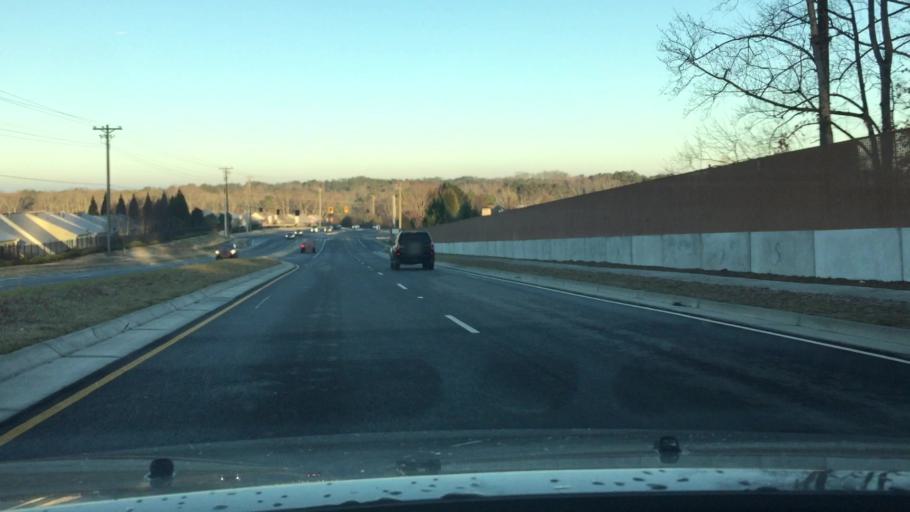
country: US
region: Georgia
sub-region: Forsyth County
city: Cumming
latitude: 34.1752
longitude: -84.1900
